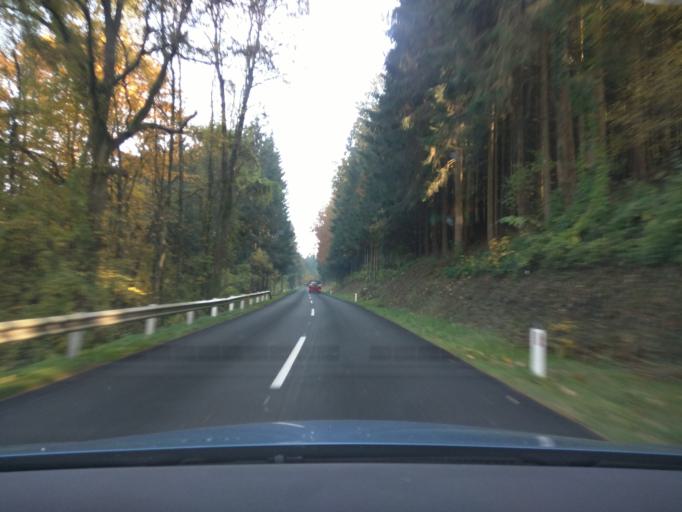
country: DE
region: Bavaria
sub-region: Lower Bavaria
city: Thyrnau
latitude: 48.5663
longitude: 13.5523
